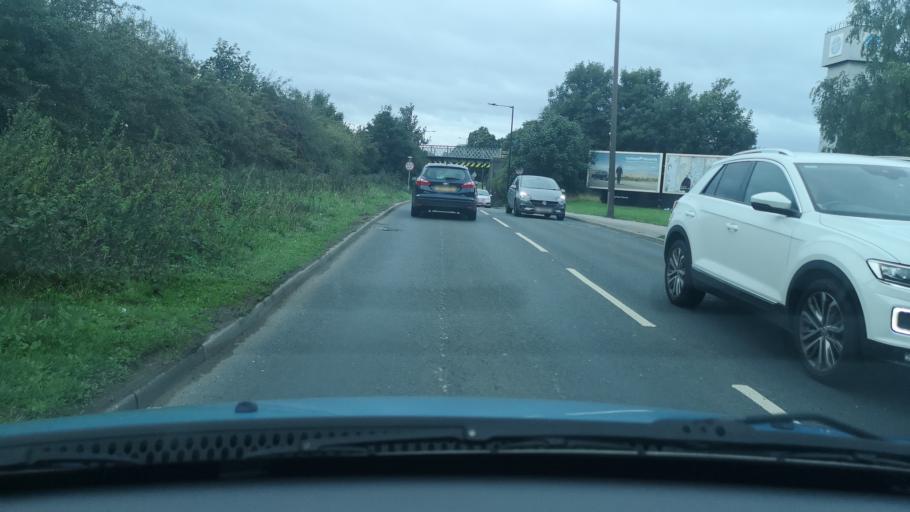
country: GB
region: England
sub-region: Doncaster
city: Kirk Sandall
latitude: 53.5533
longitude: -1.0832
